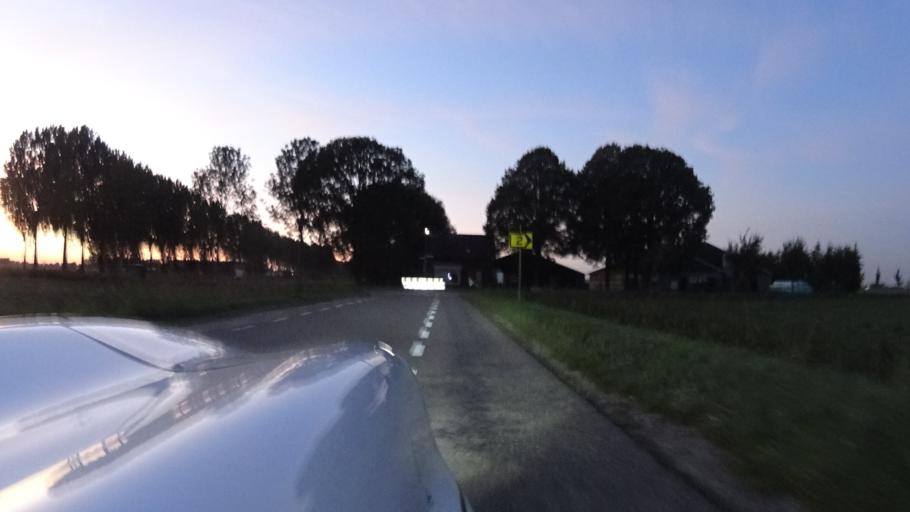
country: NL
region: North Brabant
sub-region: Gemeente Aalburg
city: Aalburg
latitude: 51.7565
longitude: 5.0805
